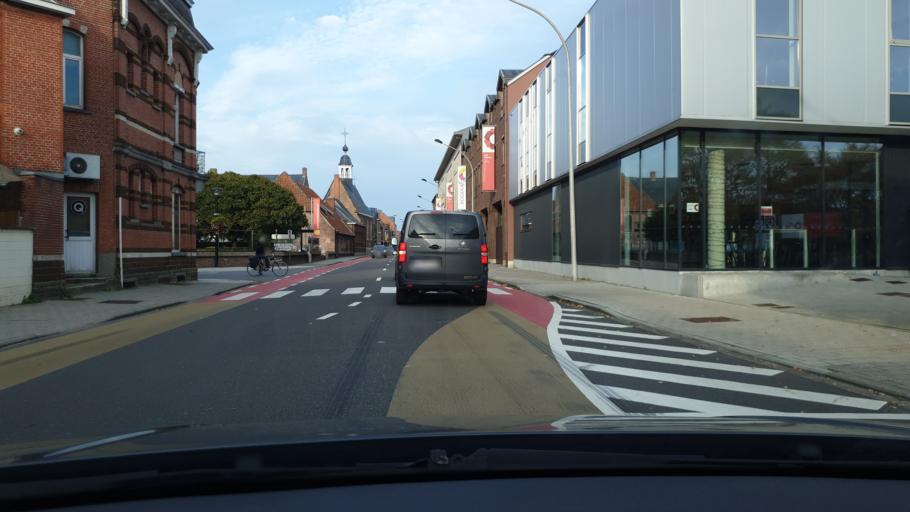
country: BE
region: Flanders
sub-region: Provincie Antwerpen
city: Geel
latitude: 51.1612
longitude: 4.9988
